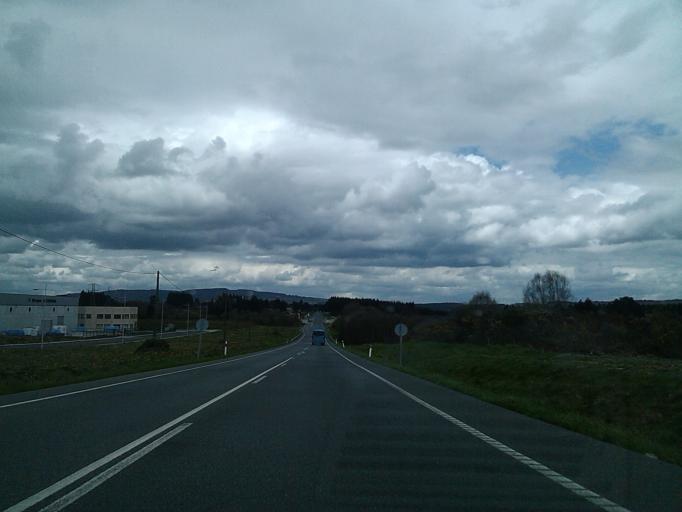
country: ES
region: Galicia
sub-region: Provincia da Coruna
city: Curtis
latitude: 43.1542
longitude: -8.0081
